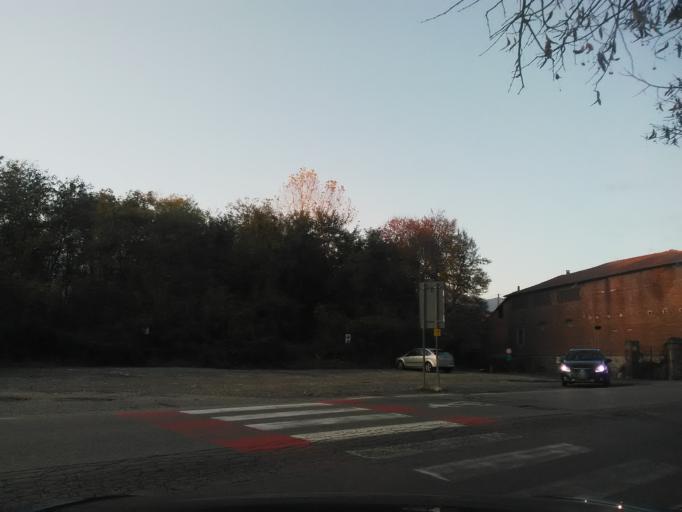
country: IT
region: Piedmont
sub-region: Provincia di Biella
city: Occhieppo Inferiore
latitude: 45.5525
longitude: 8.0166
